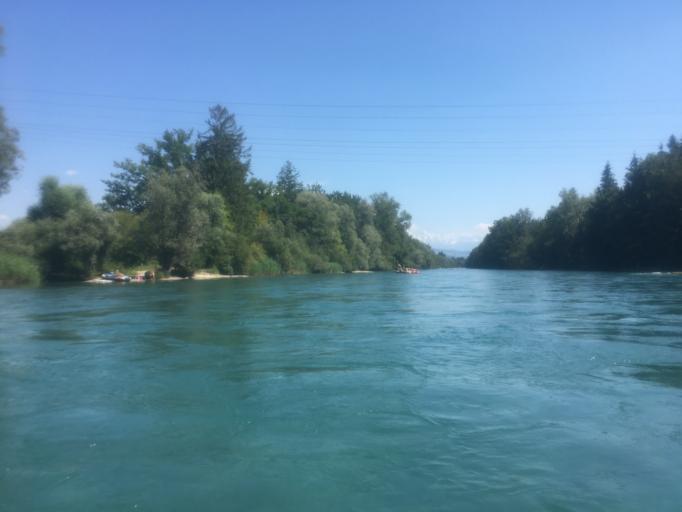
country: CH
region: Bern
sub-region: Bern-Mittelland District
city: Rubigen
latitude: 46.9041
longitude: 7.5230
